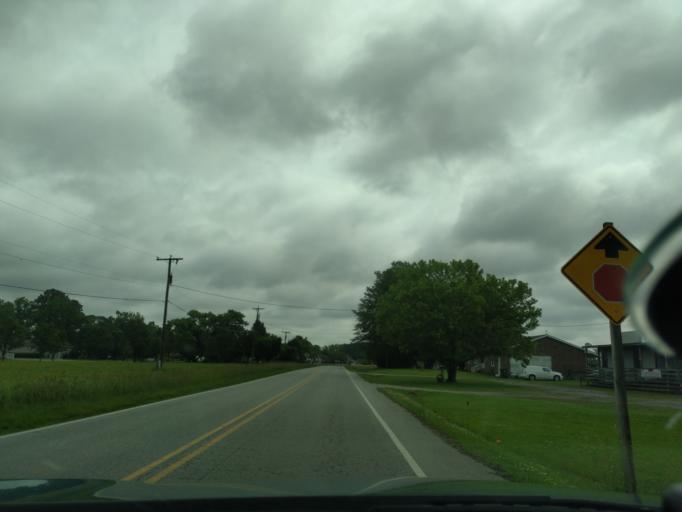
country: US
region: North Carolina
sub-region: Washington County
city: Plymouth
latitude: 35.8689
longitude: -76.7004
